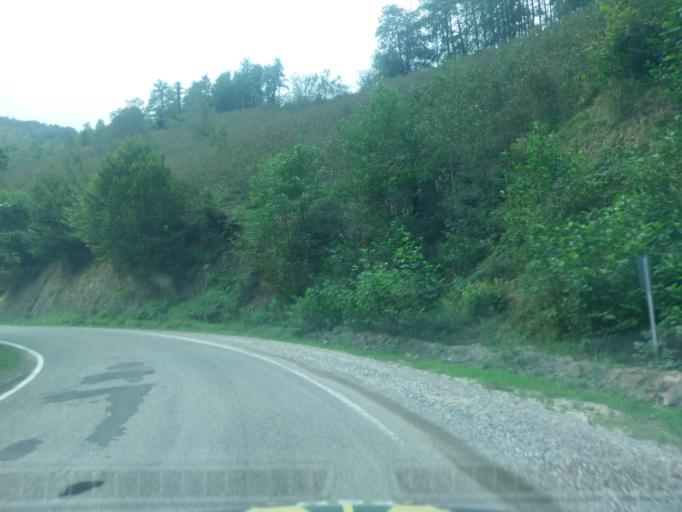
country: TR
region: Ordu
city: Gurgentepe
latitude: 40.8678
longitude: 37.6404
